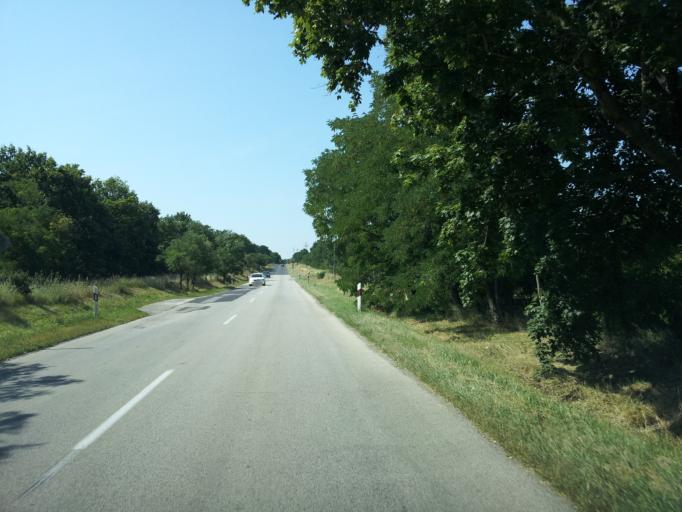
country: HU
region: Fejer
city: Pakozd
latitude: 47.2507
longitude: 18.5130
